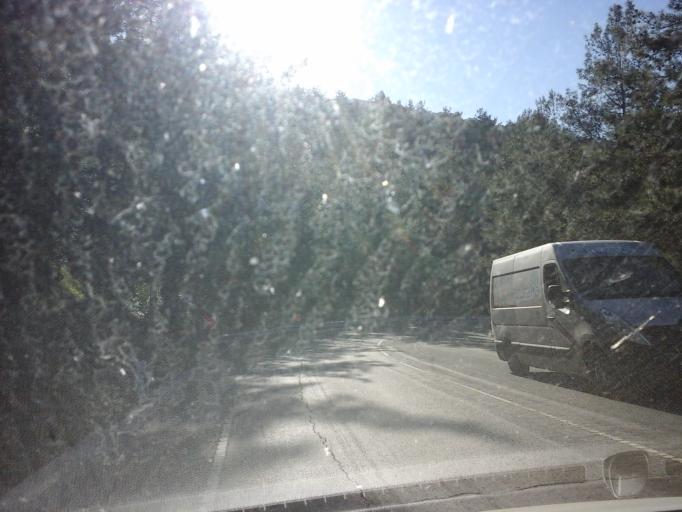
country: CY
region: Limassol
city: Kyperounta
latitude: 34.9429
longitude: 32.9296
